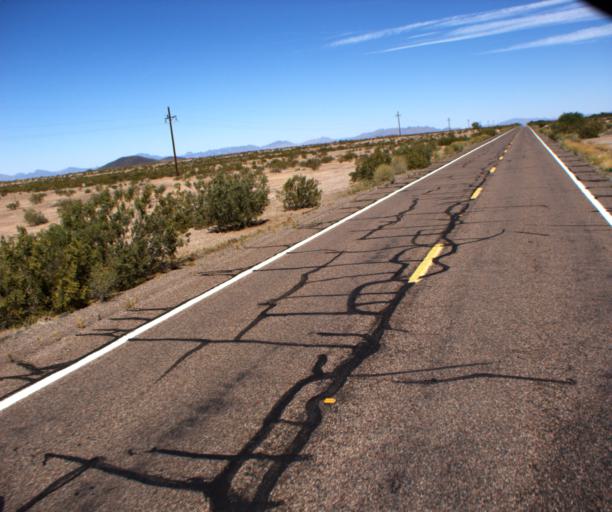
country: US
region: Arizona
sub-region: Maricopa County
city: Gila Bend
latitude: 32.7860
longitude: -112.8074
